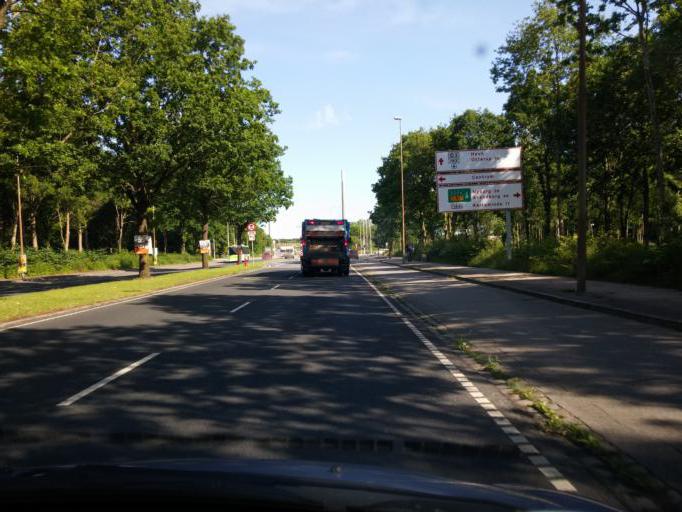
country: DK
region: South Denmark
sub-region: Odense Kommune
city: Seden
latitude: 55.4152
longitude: 10.4218
